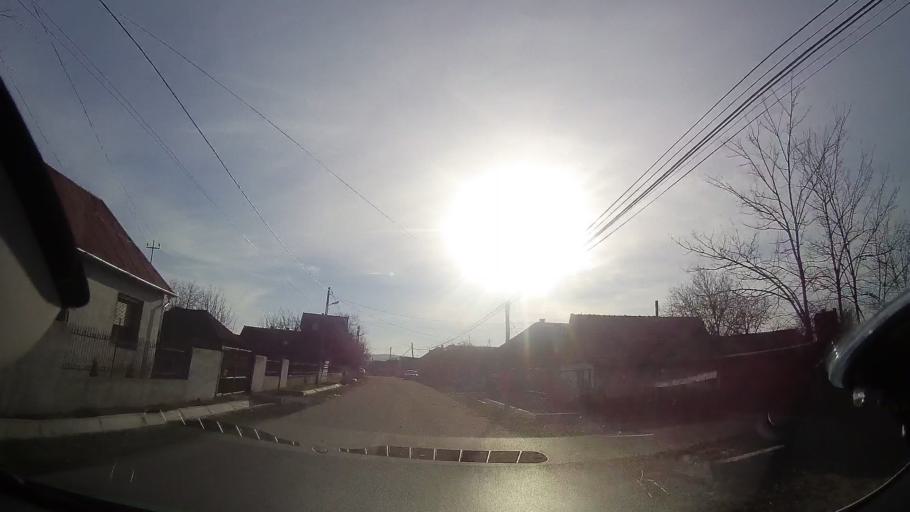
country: RO
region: Bihor
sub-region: Comuna Sarbi
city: Sarbi
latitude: 47.2058
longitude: 22.1299
